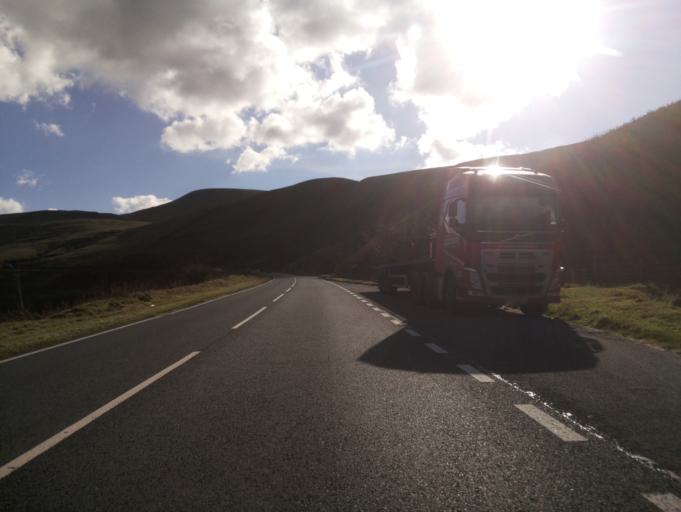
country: GB
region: Wales
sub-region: Sir Powys
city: Cray
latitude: 51.8809
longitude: -3.4945
